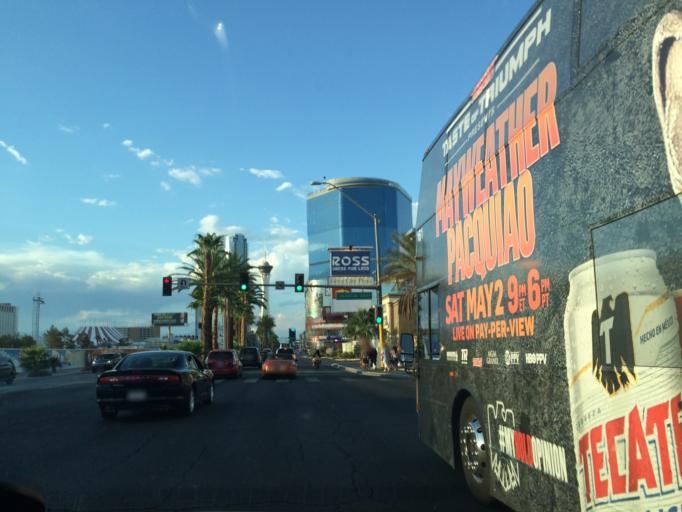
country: US
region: Nevada
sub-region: Clark County
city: Paradise
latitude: 36.1324
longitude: -115.1646
